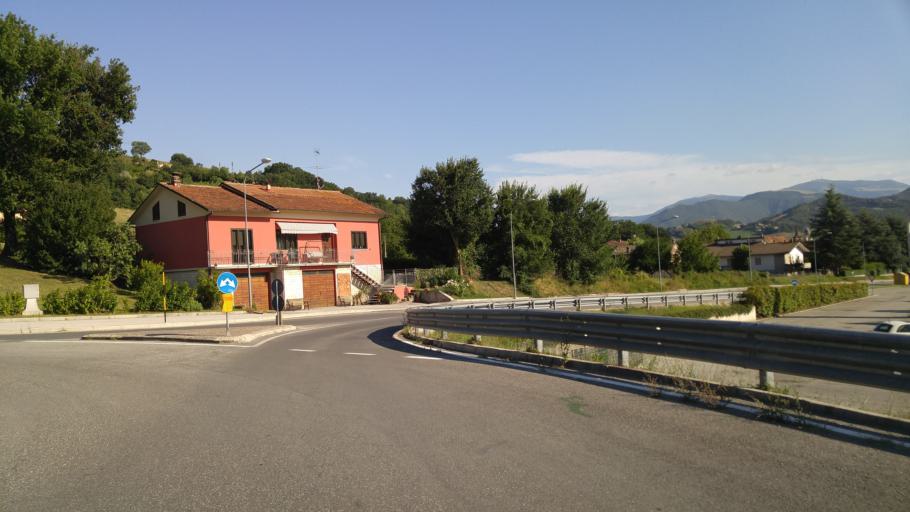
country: IT
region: The Marches
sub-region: Provincia di Pesaro e Urbino
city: Urbania
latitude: 43.6752
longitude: 12.5240
